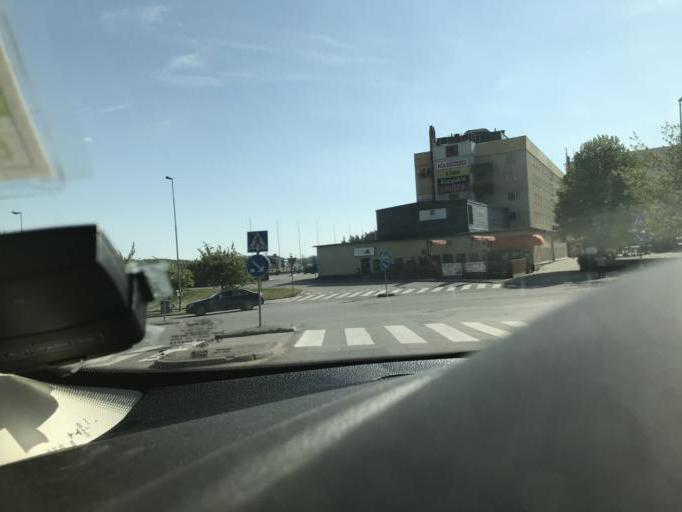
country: SE
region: Stockholm
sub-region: Botkyrka Kommun
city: Tumba
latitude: 59.1988
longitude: 17.8310
